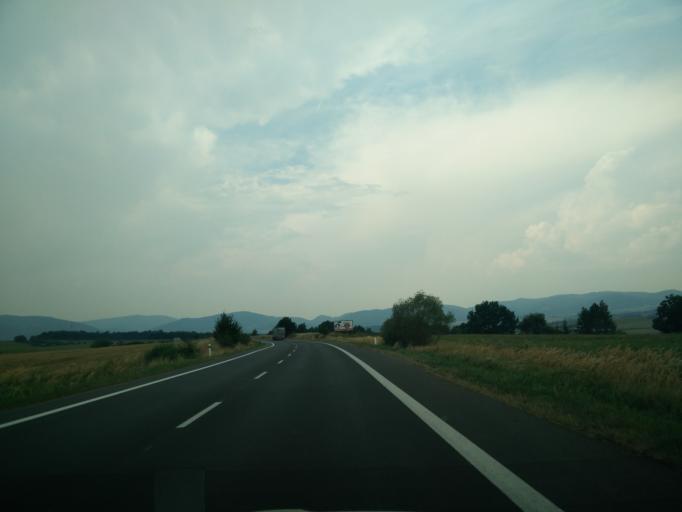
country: SK
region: Banskobystricky
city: Ziar nad Hronom
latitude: 48.6057
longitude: 18.8372
